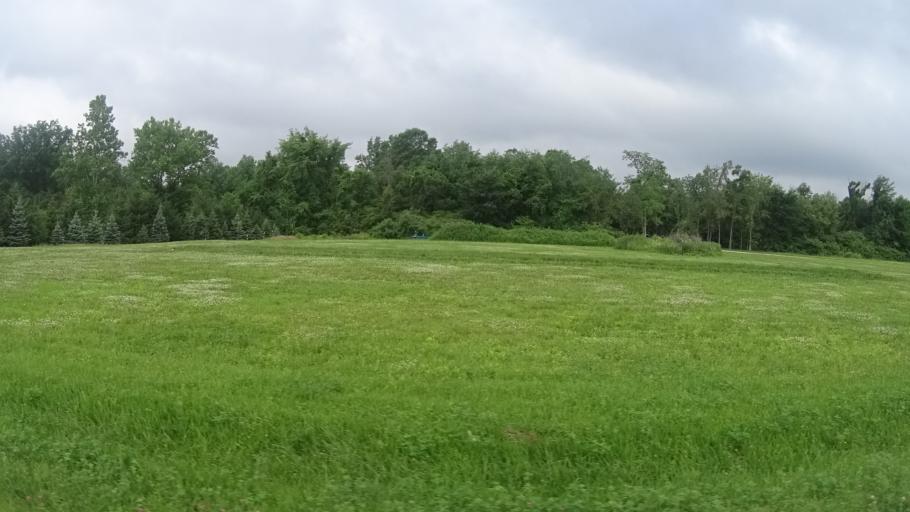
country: US
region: Ohio
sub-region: Erie County
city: Huron
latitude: 41.3415
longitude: -82.5100
